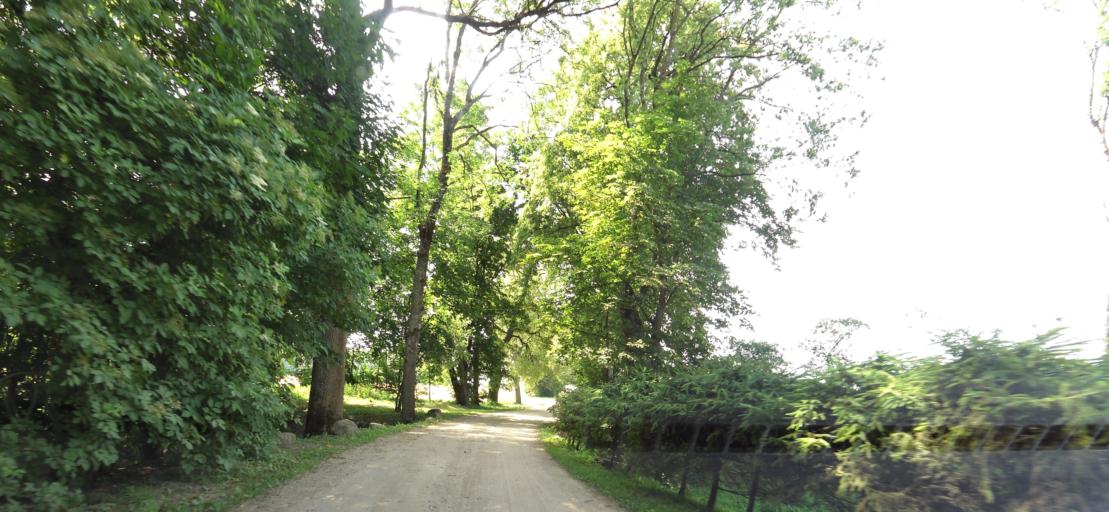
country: LT
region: Panevezys
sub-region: Birzai
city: Birzai
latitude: 56.2145
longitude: 24.6815
